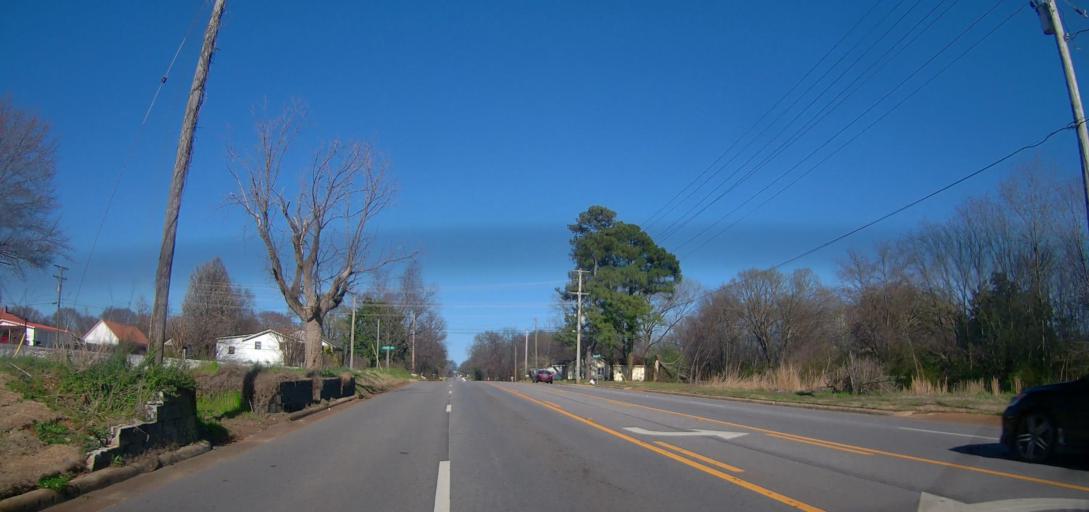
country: US
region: Alabama
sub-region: Lauderdale County
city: East Florence
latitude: 34.8049
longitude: -87.6475
